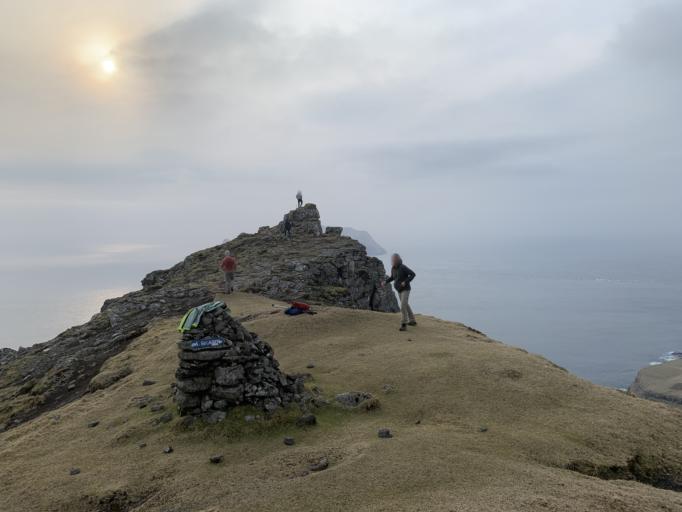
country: FO
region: Vagar
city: Sorvagur
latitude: 62.1027
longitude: -7.4216
